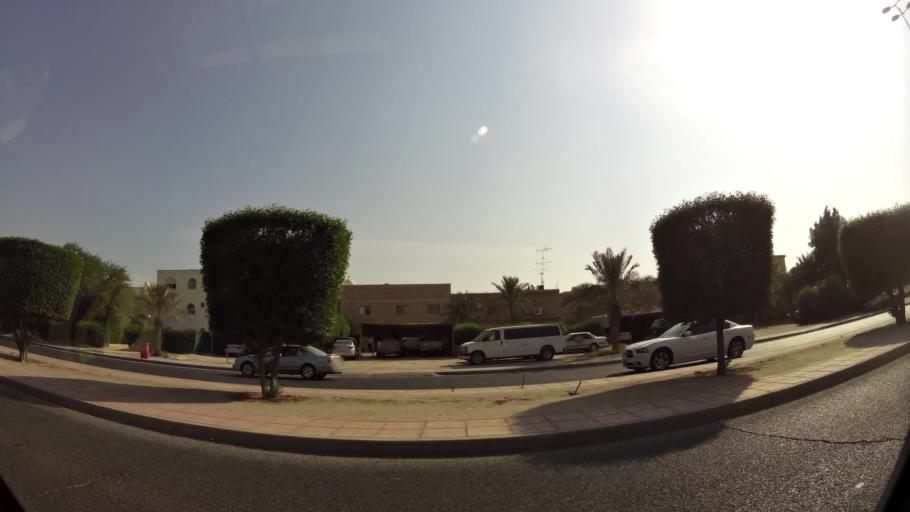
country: KW
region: Al Ahmadi
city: Ar Riqqah
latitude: 29.1589
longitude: 48.0994
